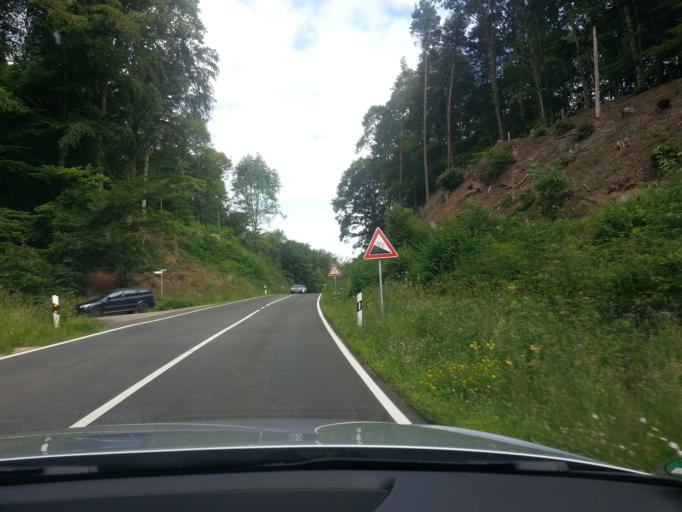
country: DE
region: Saarland
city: Losheim
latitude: 49.4721
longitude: 6.7934
